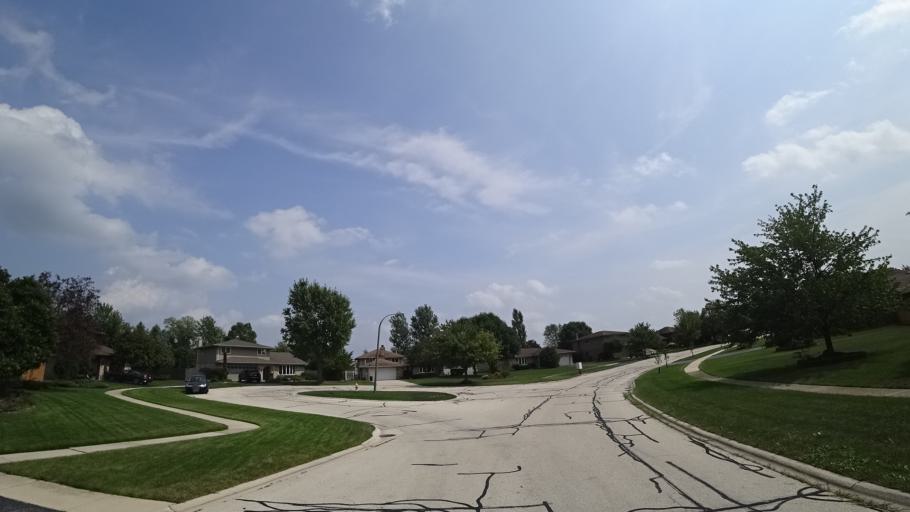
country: US
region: Illinois
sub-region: Will County
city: Goodings Grove
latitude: 41.6280
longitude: -87.9040
